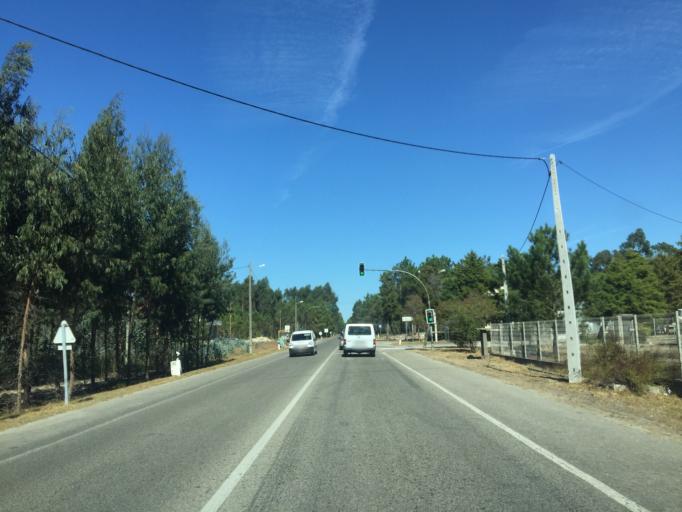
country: PT
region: Coimbra
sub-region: Figueira da Foz
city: Alhadas
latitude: 40.2913
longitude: -8.7656
